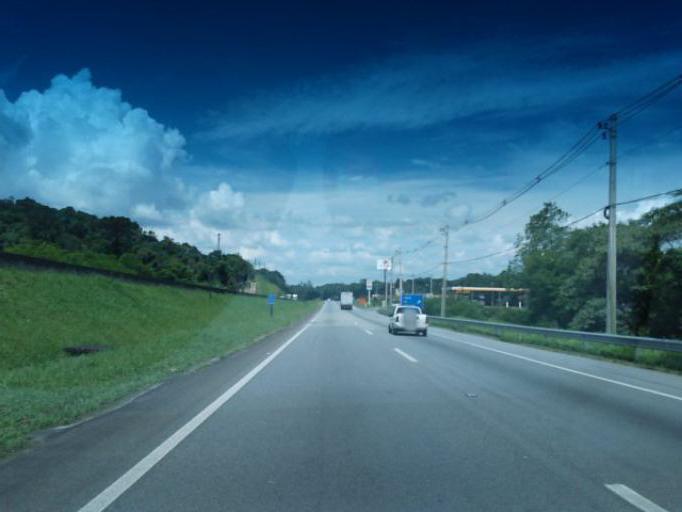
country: BR
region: Sao Paulo
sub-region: Juquitiba
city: Juquitiba
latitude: -23.9349
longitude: -47.0270
